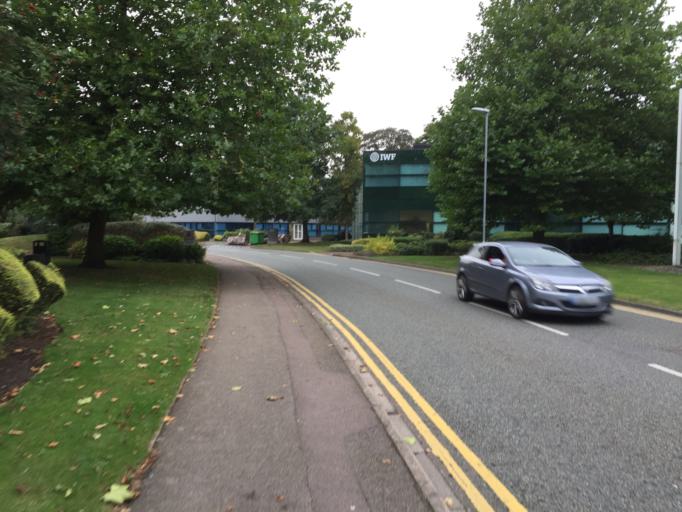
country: GB
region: England
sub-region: Cambridgeshire
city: Histon
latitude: 52.2445
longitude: 0.1084
